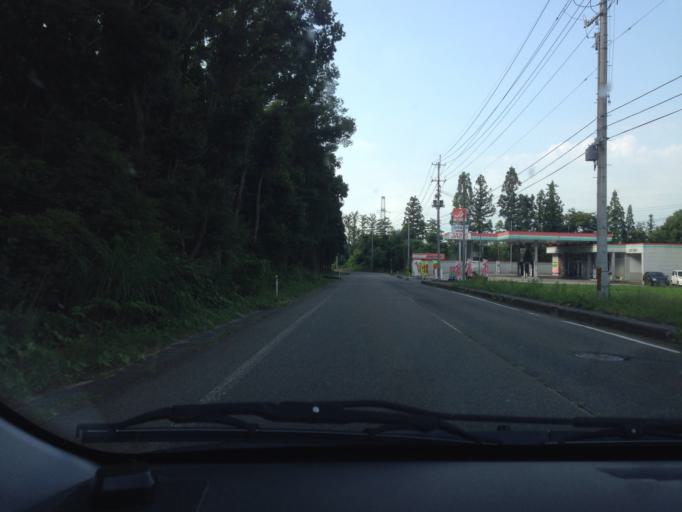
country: JP
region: Fukushima
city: Kitakata
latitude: 37.7112
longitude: 139.8789
